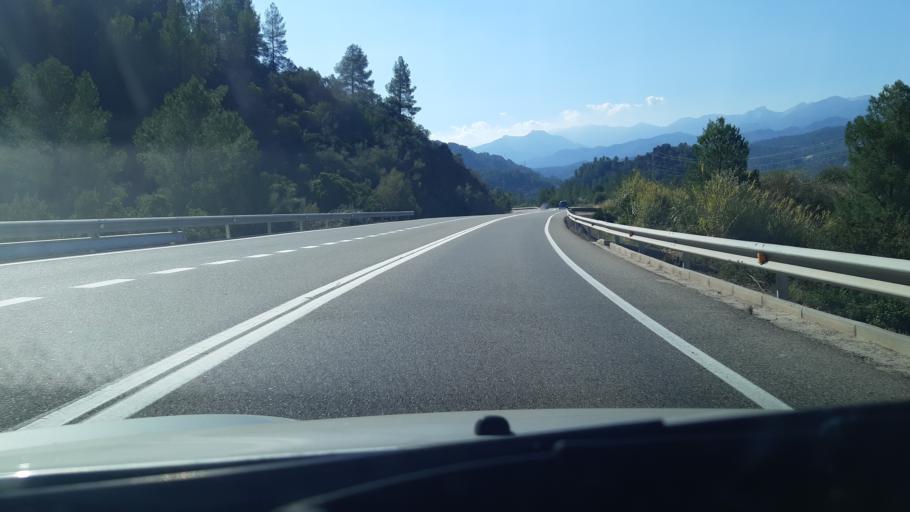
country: ES
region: Catalonia
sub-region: Provincia de Tarragona
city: Benifallet
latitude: 40.9888
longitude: 0.5406
